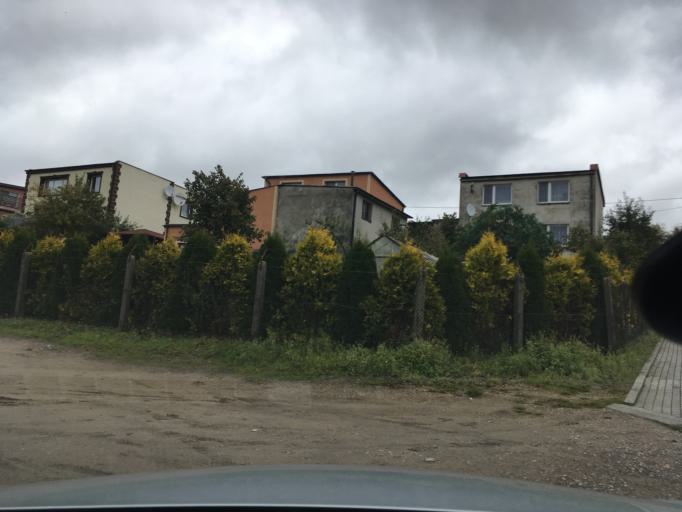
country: PL
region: Pomeranian Voivodeship
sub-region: Powiat koscierski
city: Koscierzyna
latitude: 54.1189
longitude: 17.9872
